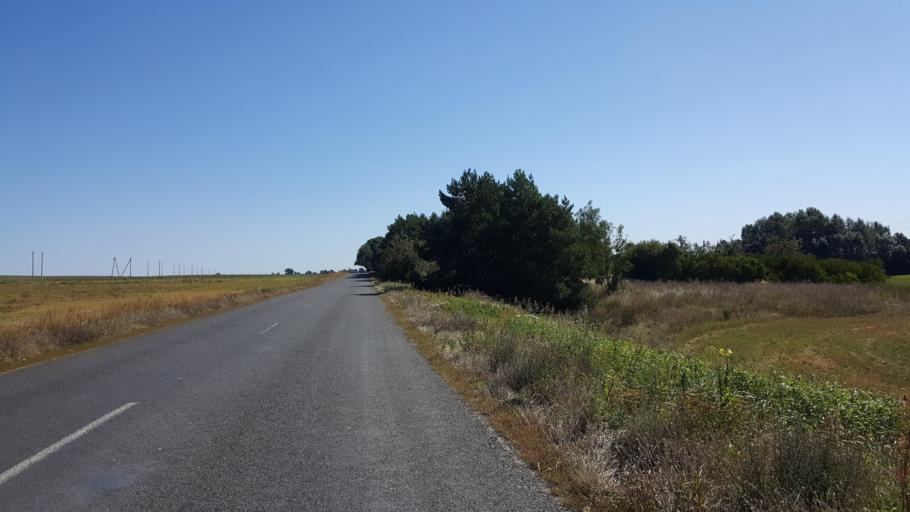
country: PL
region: Lublin Voivodeship
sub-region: Powiat bialski
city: Terespol
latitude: 52.2126
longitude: 23.5171
